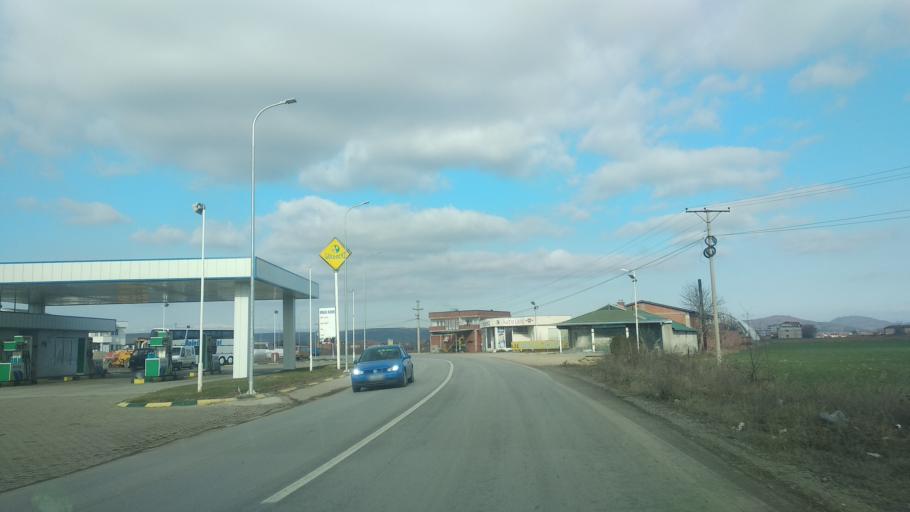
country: XK
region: Pristina
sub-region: Komuna e Obiliqit
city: Obiliq
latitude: 42.7208
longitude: 21.0966
